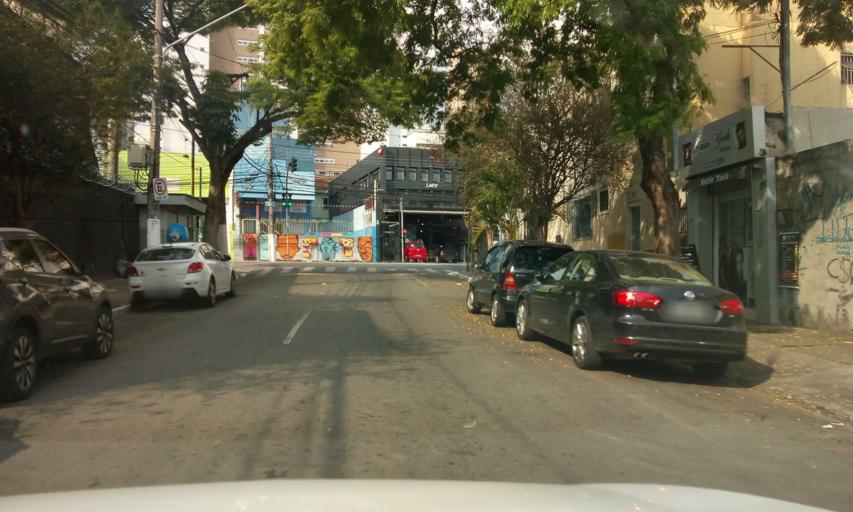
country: BR
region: Sao Paulo
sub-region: Osasco
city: Osasco
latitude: -23.5332
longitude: -46.7295
